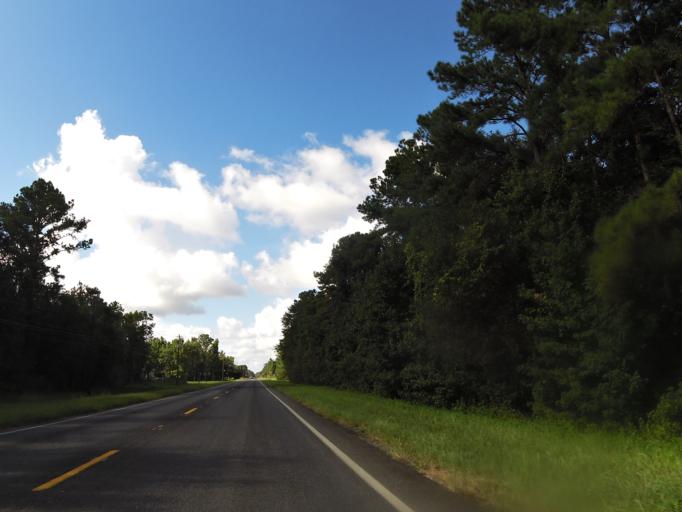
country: US
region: Georgia
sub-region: Camden County
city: Woodbine
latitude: 30.9474
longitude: -81.7195
